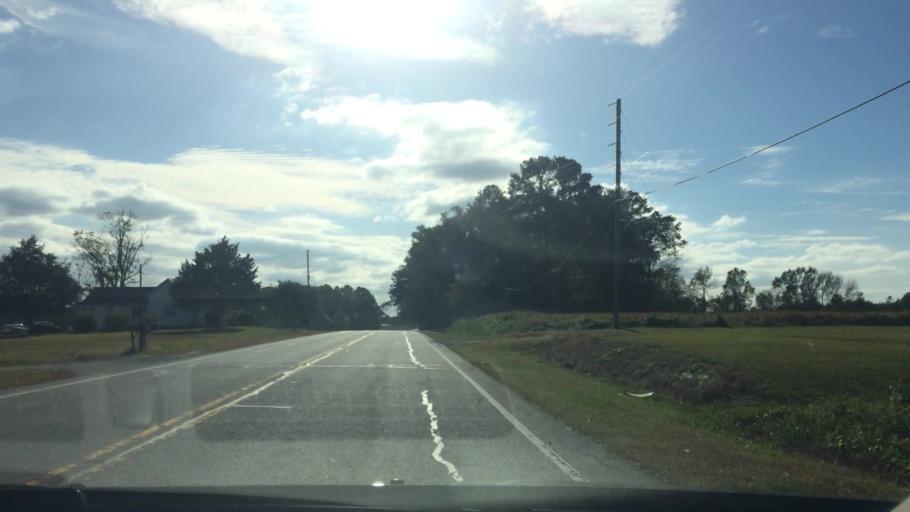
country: US
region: North Carolina
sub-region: Greene County
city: Snow Hill
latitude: 35.4526
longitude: -77.7301
